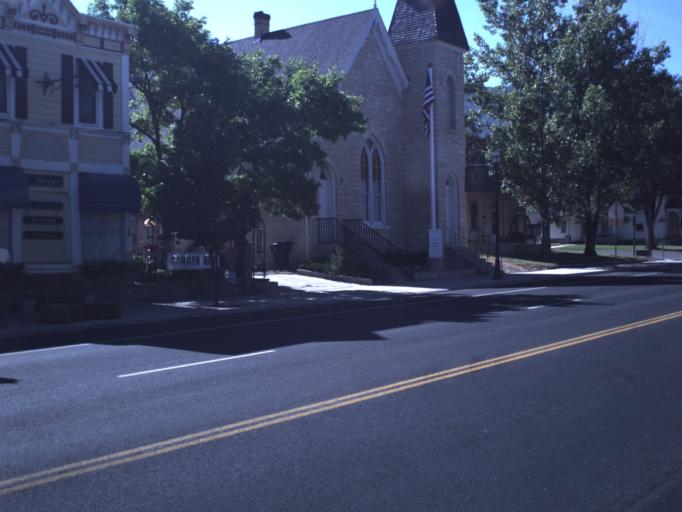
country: US
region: Utah
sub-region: Sanpete County
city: Manti
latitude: 39.2632
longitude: -111.6371
